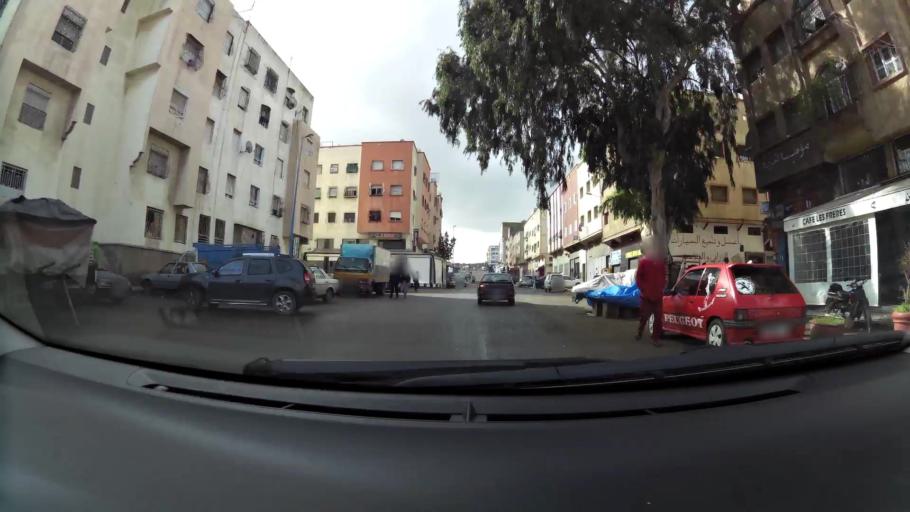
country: MA
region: Grand Casablanca
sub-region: Mediouna
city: Tit Mellil
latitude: 33.5854
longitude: -7.5224
